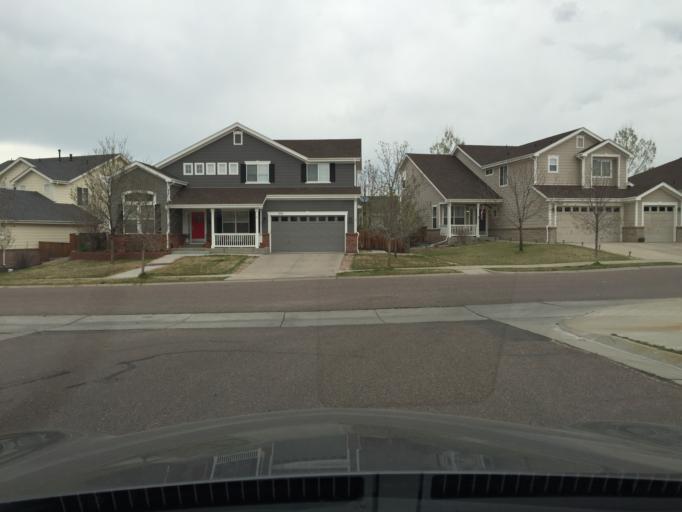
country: US
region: Colorado
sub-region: Boulder County
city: Erie
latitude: 40.0099
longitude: -105.0181
